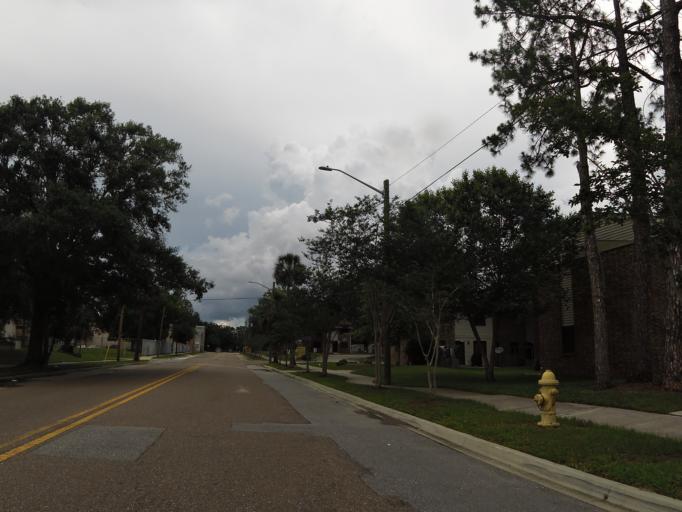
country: US
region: Florida
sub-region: Duval County
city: Jacksonville
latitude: 30.3341
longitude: -81.6505
